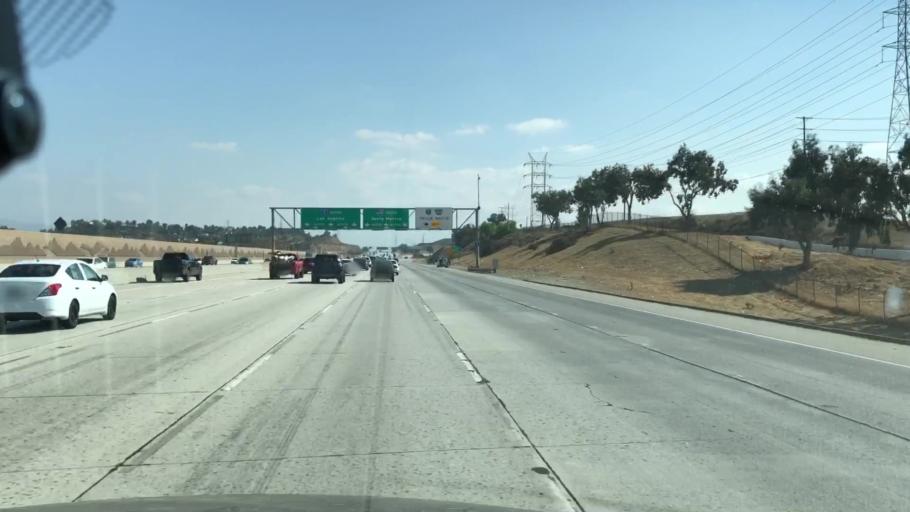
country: US
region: California
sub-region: Los Angeles County
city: San Fernando
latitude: 34.2999
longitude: -118.4767
